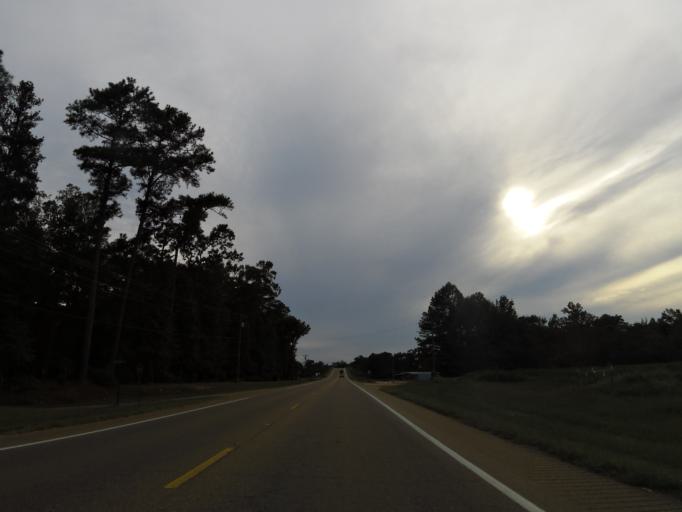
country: US
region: Alabama
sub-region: Monroe County
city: Frisco City
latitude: 31.4428
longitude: -87.3892
